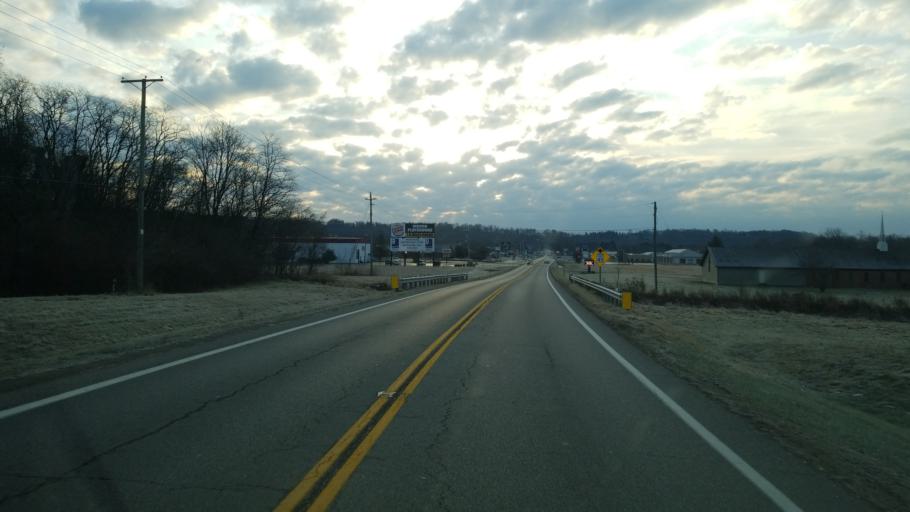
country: US
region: Ohio
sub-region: Ross County
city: North Fork Village
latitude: 39.3488
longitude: -83.0431
